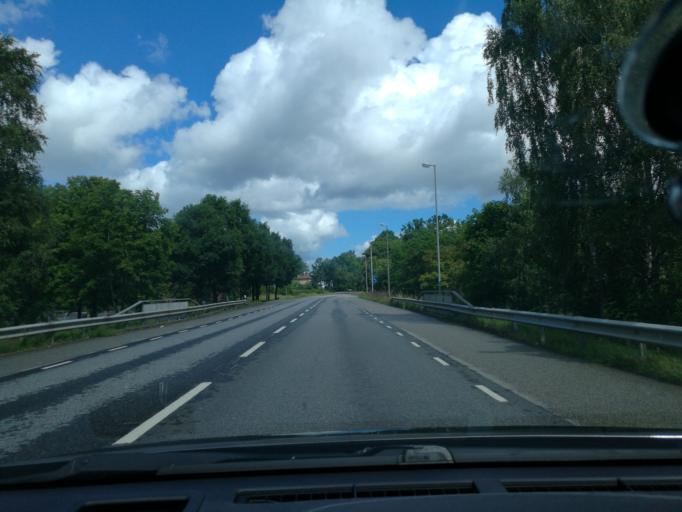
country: SE
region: Skane
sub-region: Hoors Kommun
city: Hoeoer
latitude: 55.9324
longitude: 13.5521
